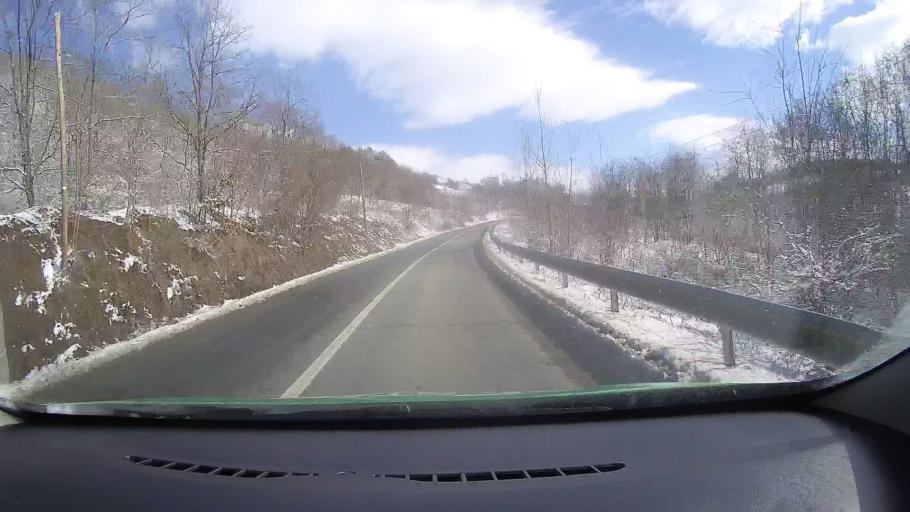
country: RO
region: Sibiu
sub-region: Comuna Barghis
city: Barghis
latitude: 45.9846
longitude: 24.5049
